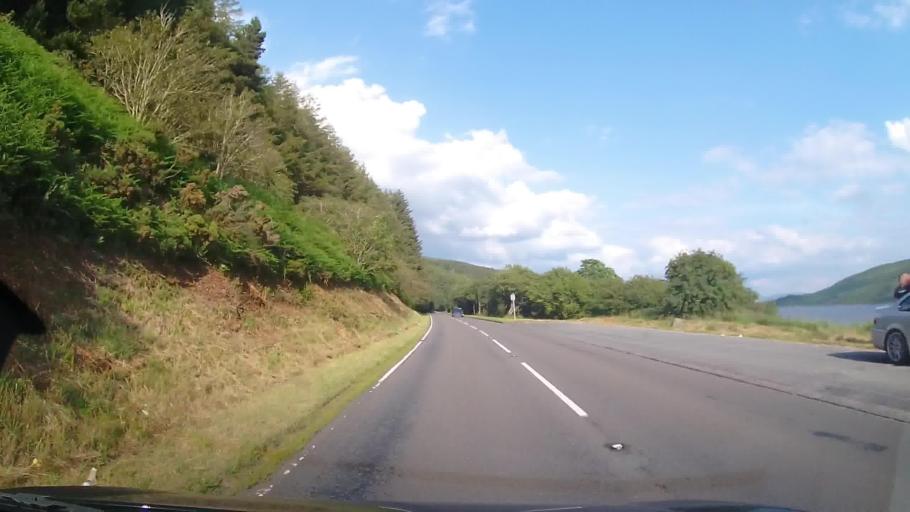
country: GB
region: Wales
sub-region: Gwynedd
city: Bala
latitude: 52.9546
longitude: -3.7034
